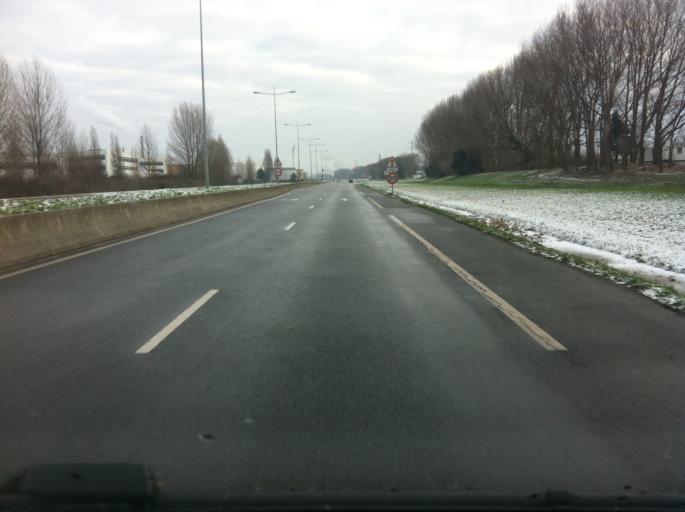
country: FR
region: Haute-Normandie
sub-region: Departement de la Seine-Maritime
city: Harfleur
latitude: 49.4863
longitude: 0.2194
